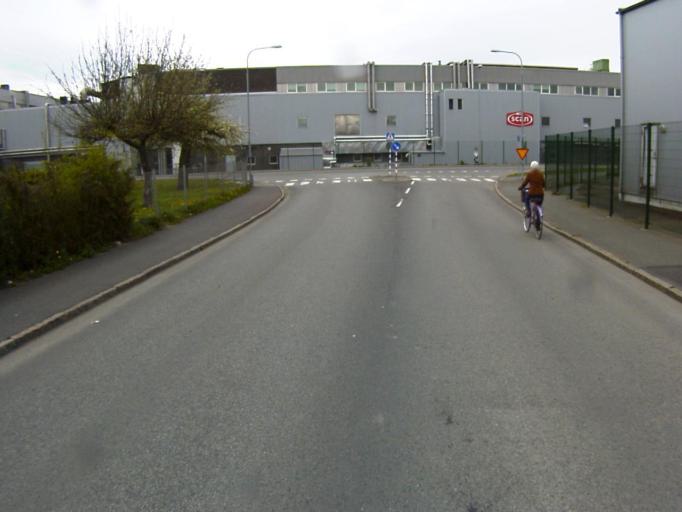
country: SE
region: Skane
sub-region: Kristianstads Kommun
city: Kristianstad
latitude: 56.0189
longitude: 14.1461
